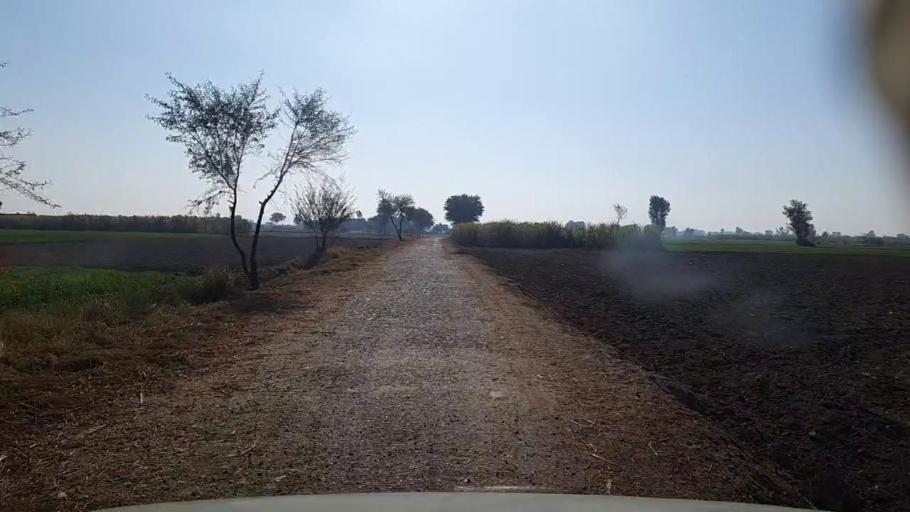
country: PK
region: Sindh
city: Khairpur
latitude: 28.0571
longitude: 69.7368
